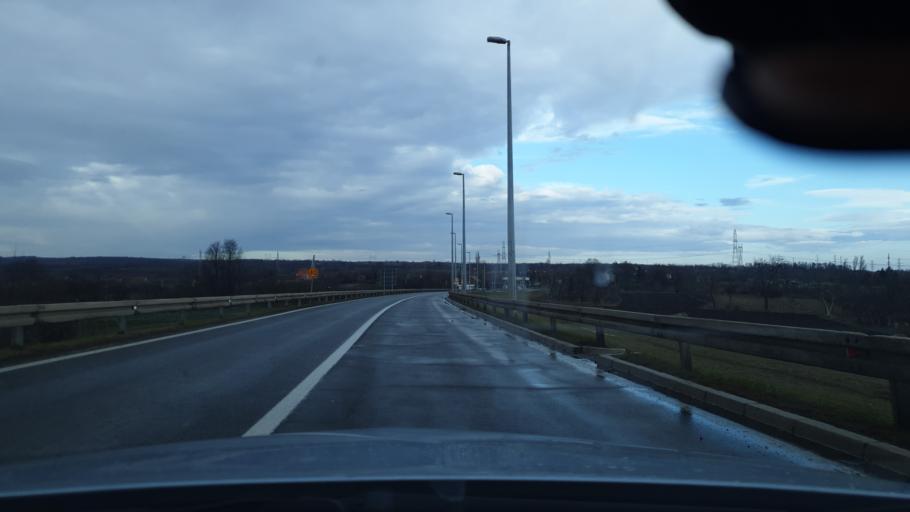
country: RS
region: Central Serbia
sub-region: Podunavski Okrug
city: Smederevo
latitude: 44.5871
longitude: 20.9589
